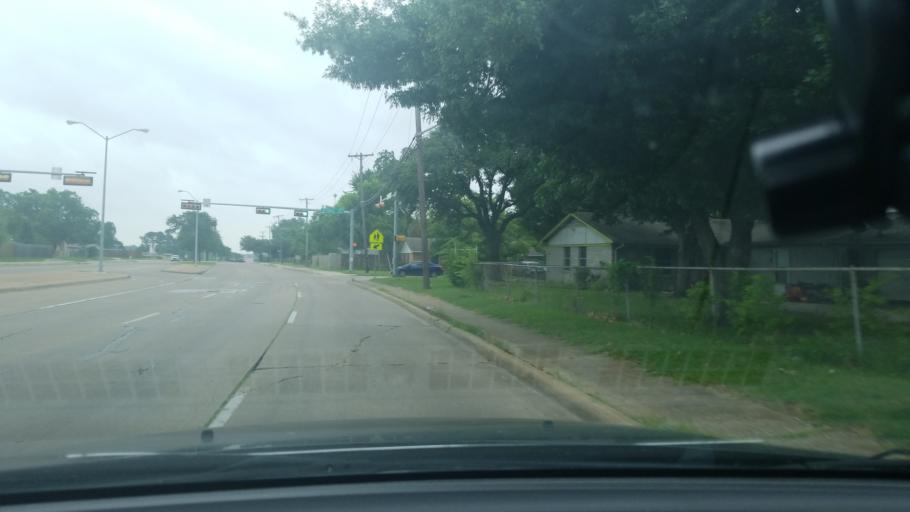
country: US
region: Texas
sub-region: Dallas County
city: Mesquite
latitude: 32.7891
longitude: -96.6332
